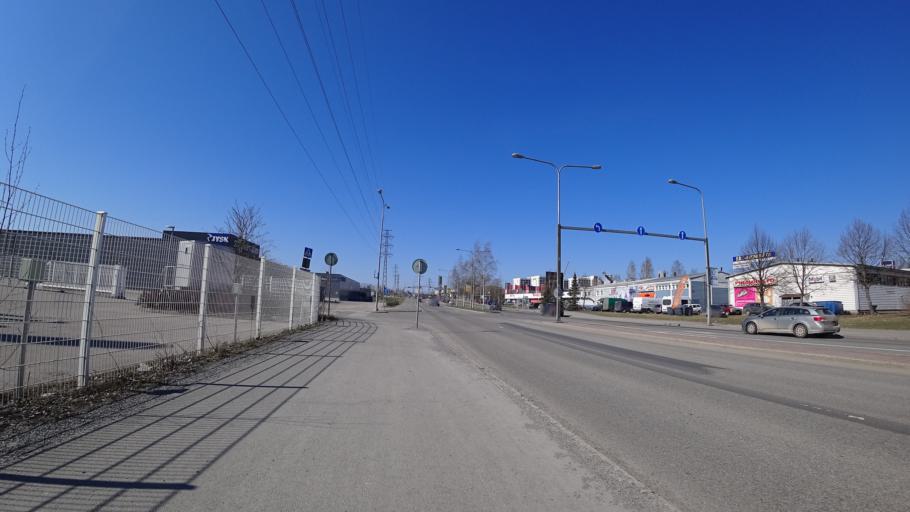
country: FI
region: Pirkanmaa
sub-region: Tampere
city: Pirkkala
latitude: 61.5164
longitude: 23.6698
